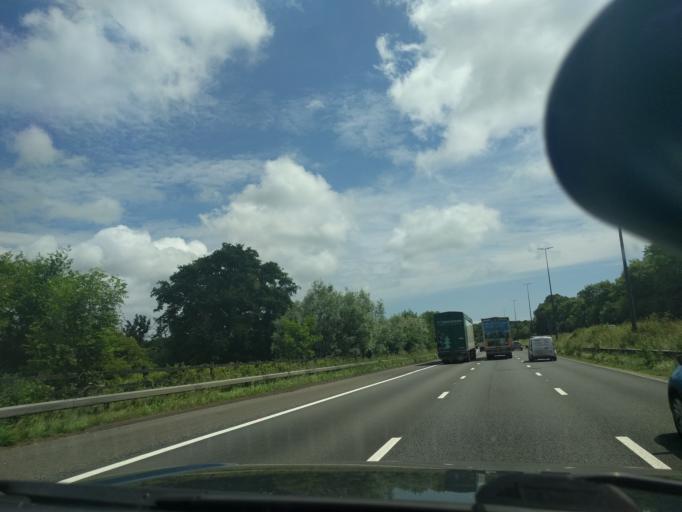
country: GB
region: Wales
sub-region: Newport
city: Langstone
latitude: 51.6022
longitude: -2.8972
